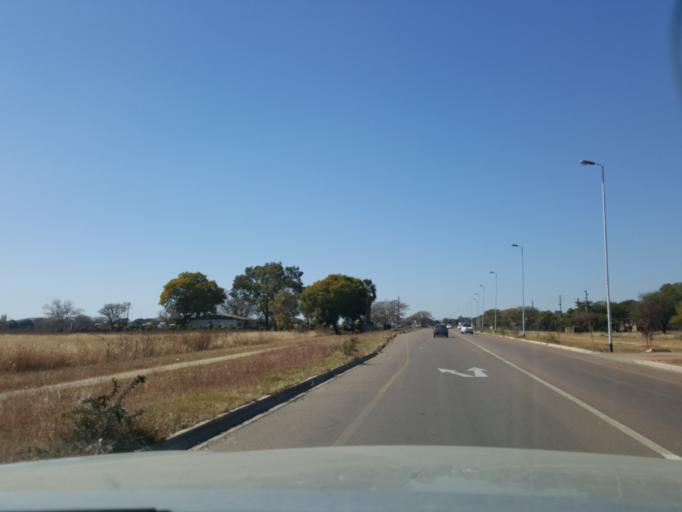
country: ZA
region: Gauteng
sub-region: City of Tshwane Metropolitan Municipality
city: Pretoria
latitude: -25.6541
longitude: 28.1990
